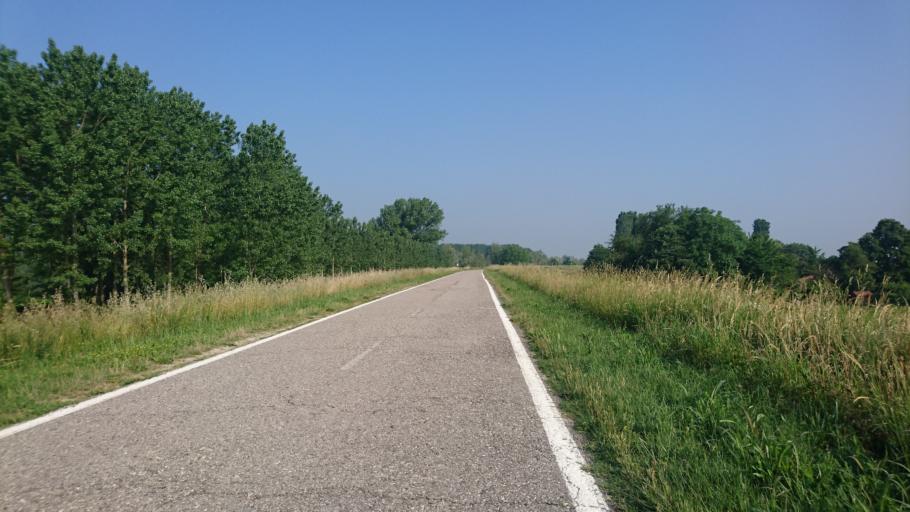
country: IT
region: Veneto
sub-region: Provincia di Rovigo
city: Castelnovo Bariano
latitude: 45.0226
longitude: 11.2750
